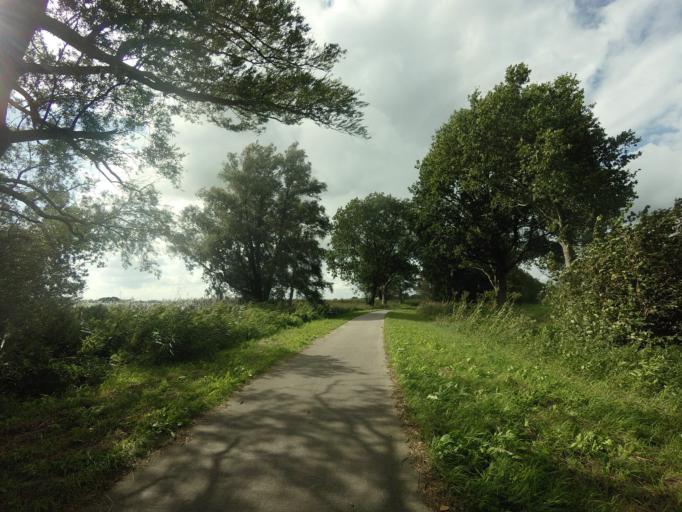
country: NL
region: Overijssel
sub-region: Gemeente Steenwijkerland
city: Blokzijl
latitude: 52.7317
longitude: 6.0105
